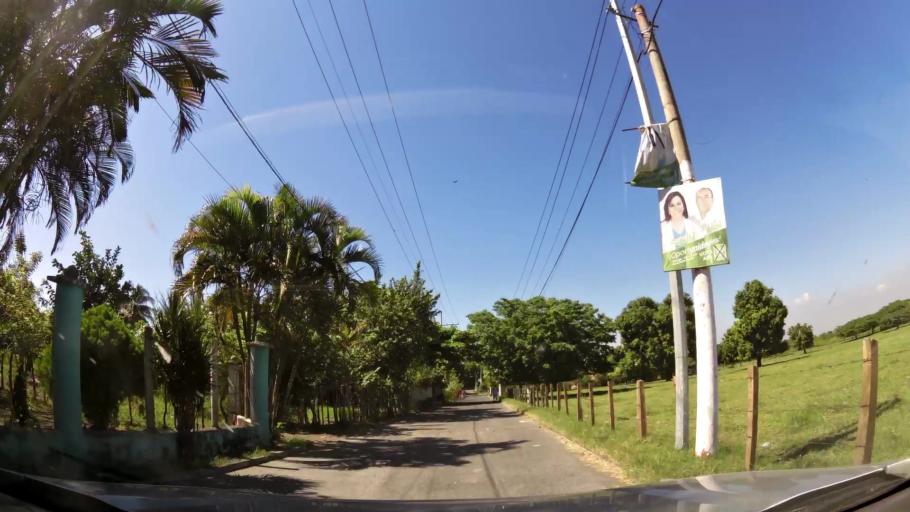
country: GT
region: Escuintla
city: Iztapa
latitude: 13.9398
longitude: -90.7132
